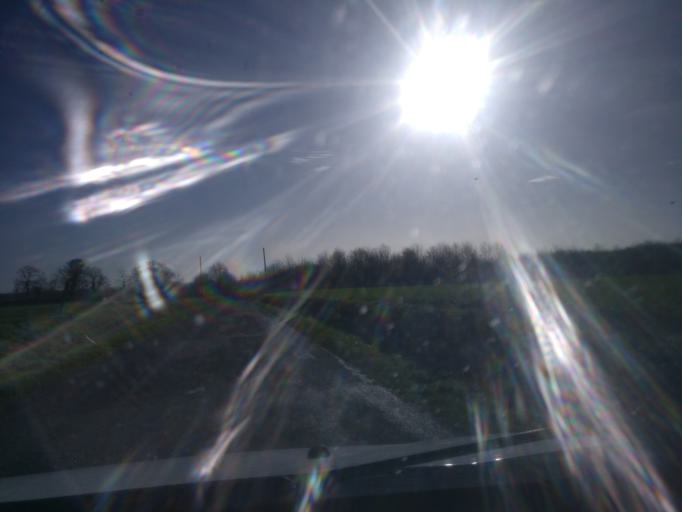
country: FR
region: Brittany
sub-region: Departement d'Ille-et-Vilaine
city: Pleine-Fougeres
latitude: 48.5327
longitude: -1.5387
